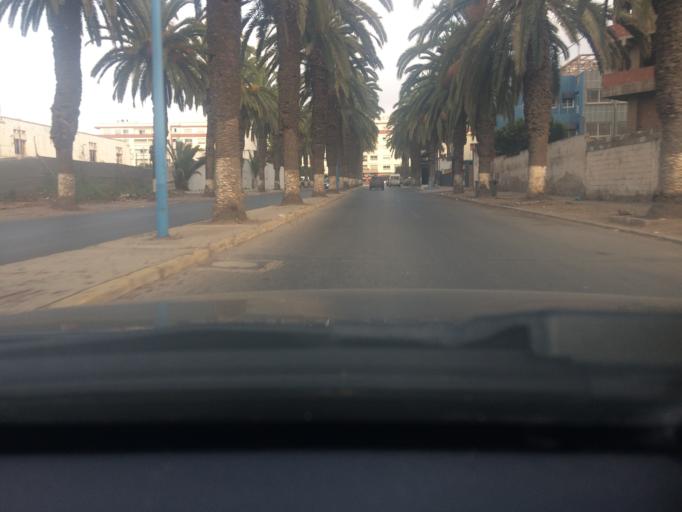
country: MA
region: Grand Casablanca
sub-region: Mohammedia
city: Mohammedia
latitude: 33.6931
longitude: -7.3950
